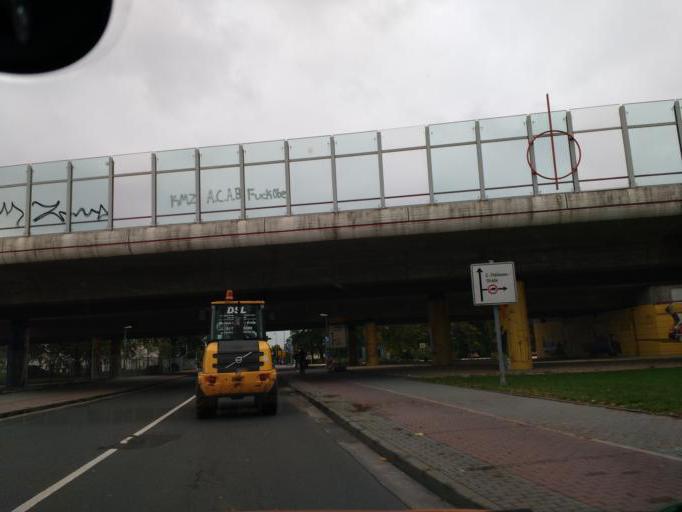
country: DE
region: Brandenburg
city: Ludwigsfelde
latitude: 52.3028
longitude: 13.2568
